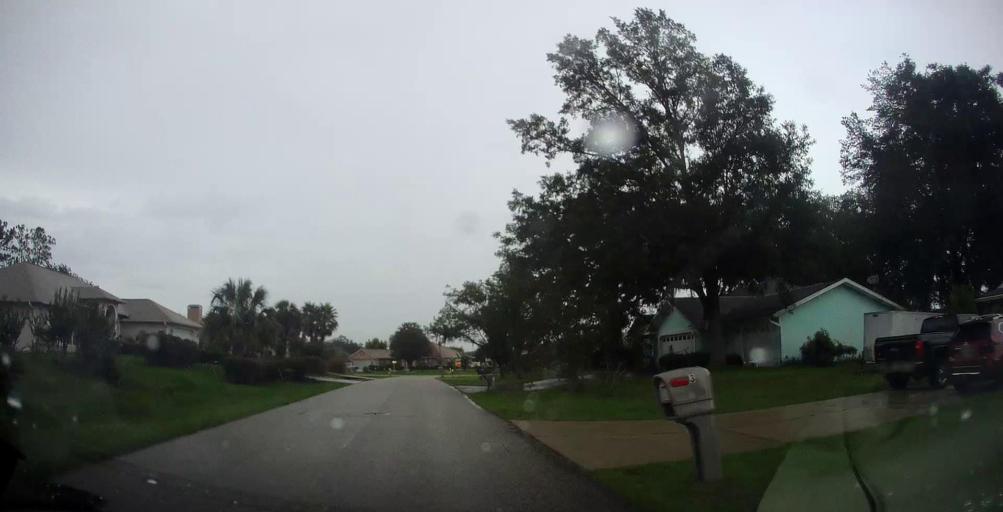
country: US
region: Florida
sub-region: Marion County
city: Silver Springs Shores
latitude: 29.1291
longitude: -82.0130
